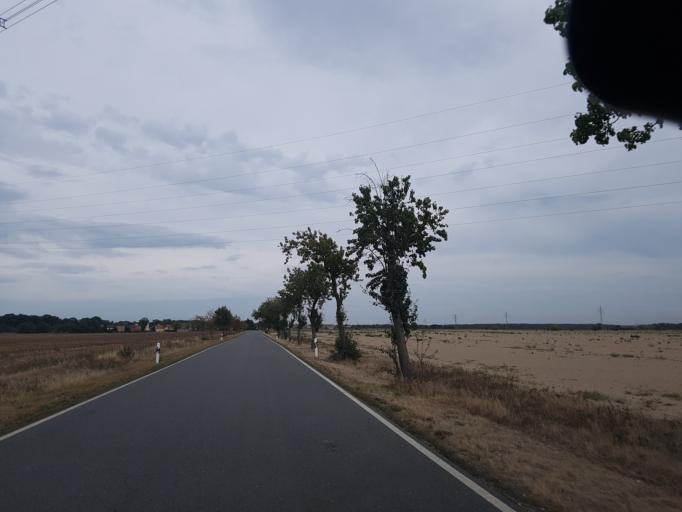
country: DE
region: Saxony-Anhalt
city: Annaburg
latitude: 51.7821
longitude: 13.0363
